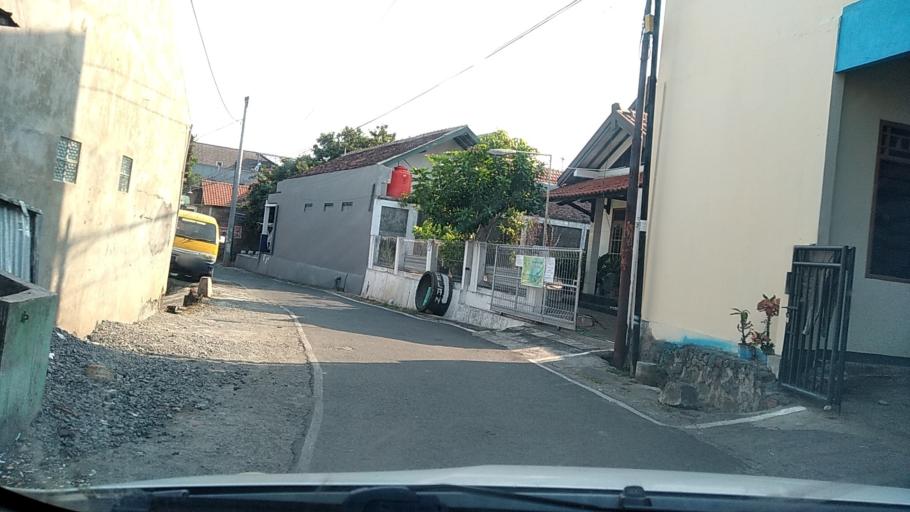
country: ID
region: Central Java
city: Semarang
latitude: -7.0580
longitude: 110.4441
